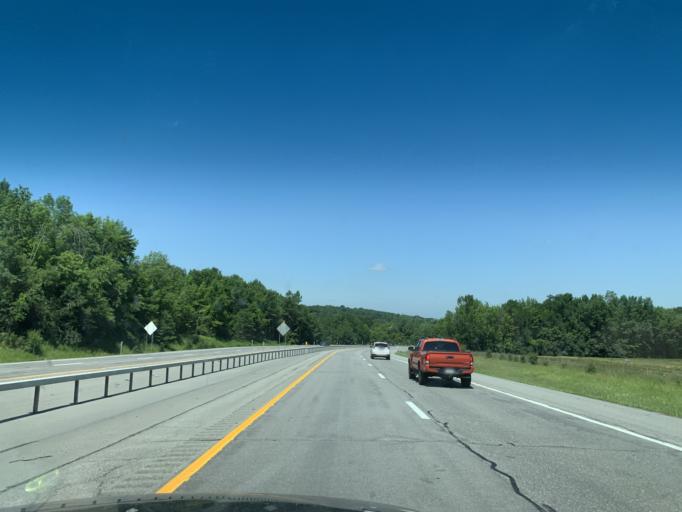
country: US
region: New York
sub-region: Oneida County
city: Chadwicks
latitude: 43.0318
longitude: -75.2682
